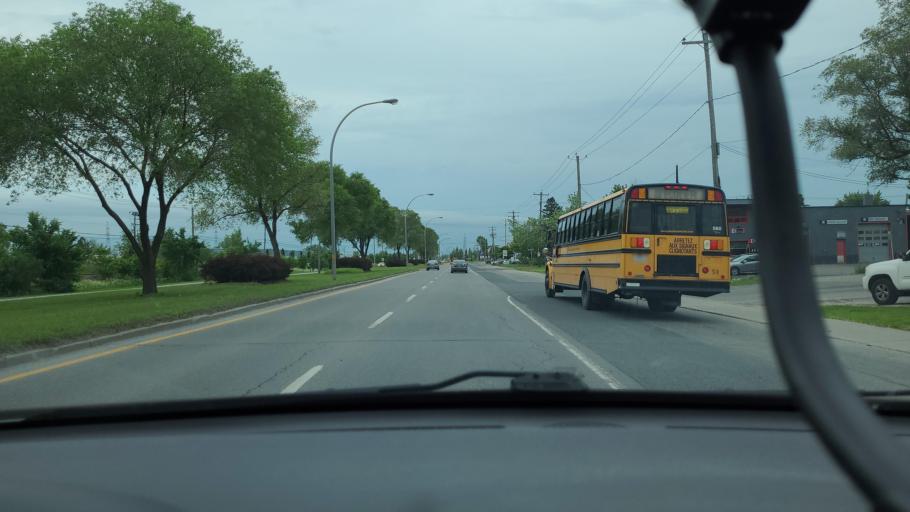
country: CA
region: Quebec
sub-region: Monteregie
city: La Prairie
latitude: 45.4021
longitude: -73.5011
